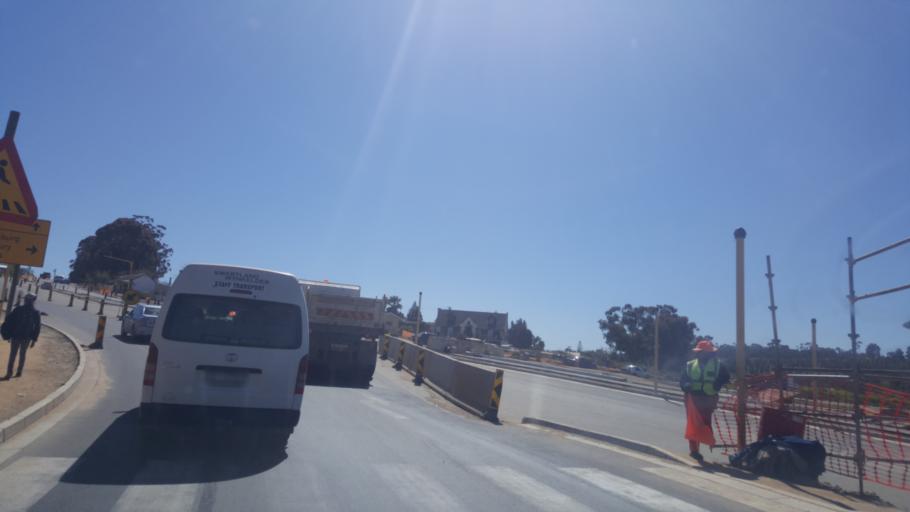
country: ZA
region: Western Cape
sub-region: West Coast District Municipality
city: Malmesbury
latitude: -33.4652
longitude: 18.7168
